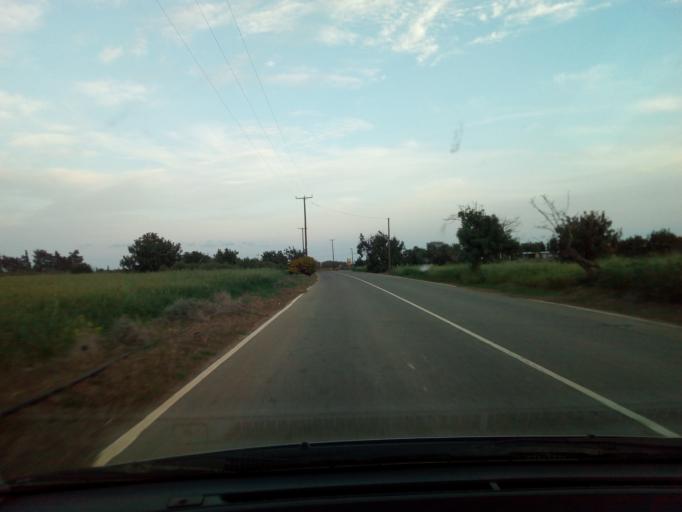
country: CY
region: Larnaka
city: Tersefanou
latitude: 34.8028
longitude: 33.5049
